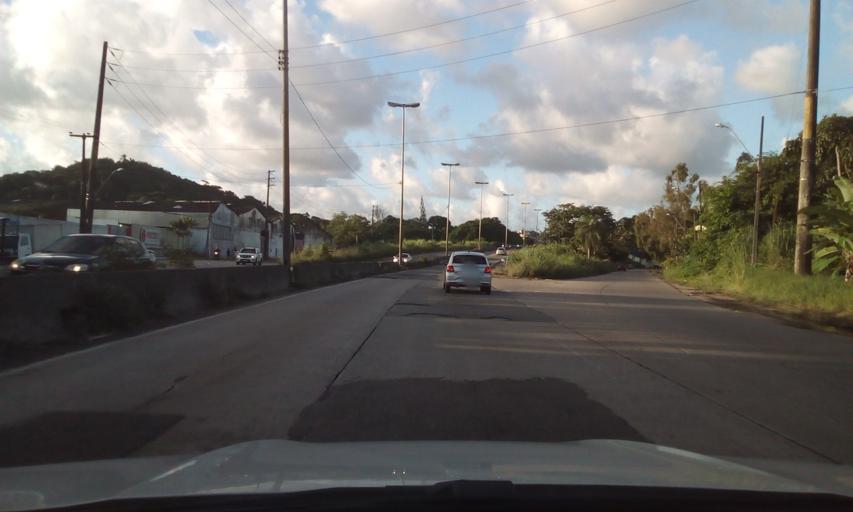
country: BR
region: Pernambuco
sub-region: Recife
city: Recife
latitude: -8.0193
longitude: -34.9423
